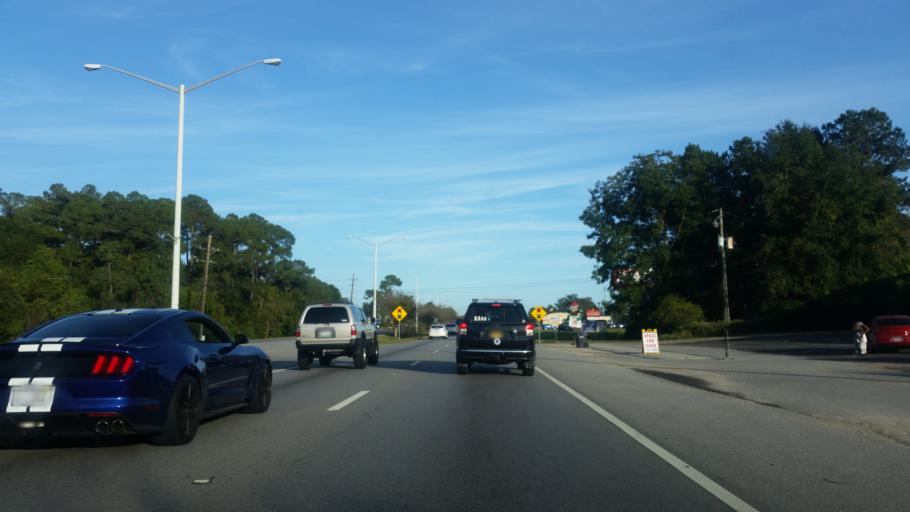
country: US
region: Mississippi
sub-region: Jackson County
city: Ocean Springs
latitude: 30.4153
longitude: -88.7991
